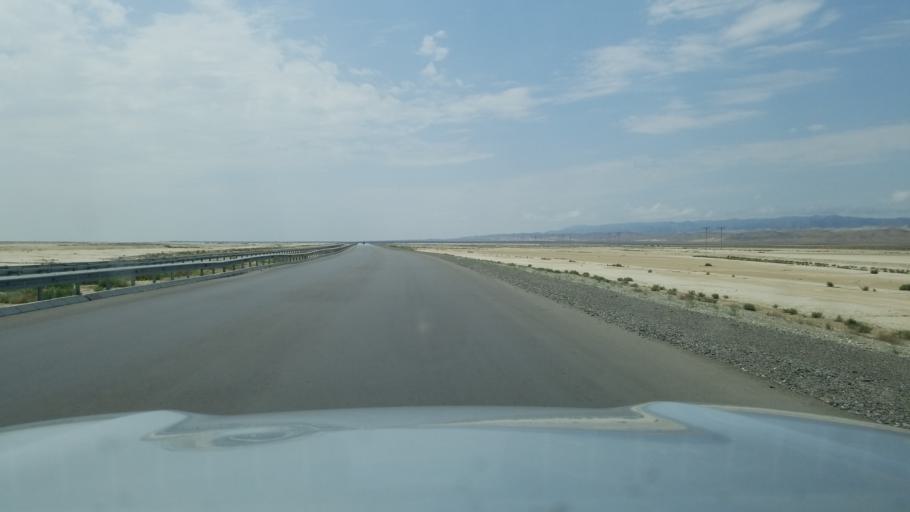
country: TM
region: Balkan
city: Gazanjyk
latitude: 39.2750
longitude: 55.1729
